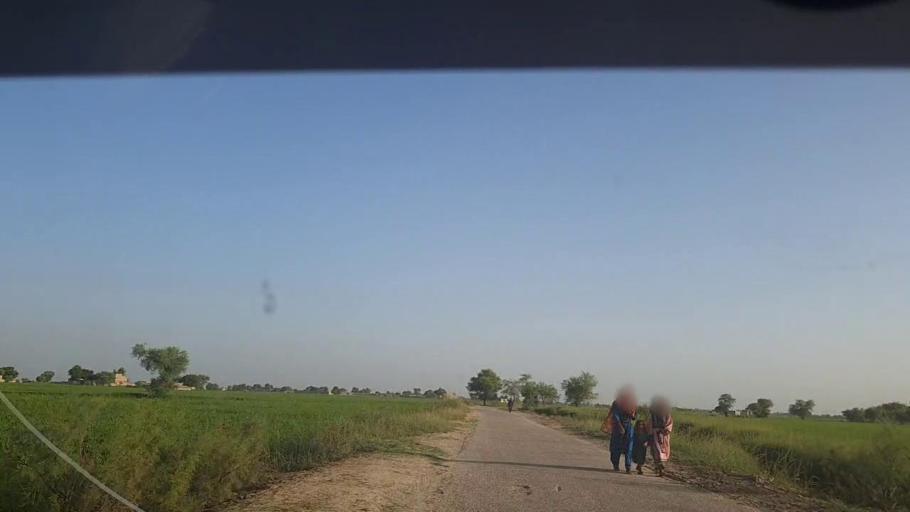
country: PK
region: Sindh
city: Thul
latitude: 28.2022
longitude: 68.8738
